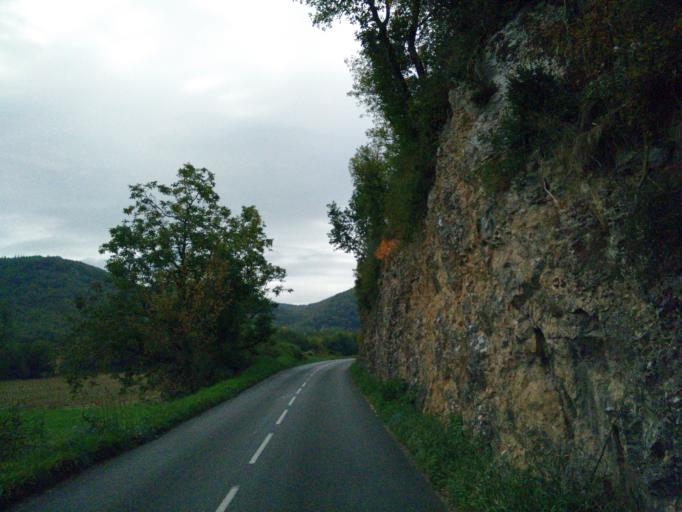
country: FR
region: Midi-Pyrenees
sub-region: Departement du Lot
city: Lalbenque
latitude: 44.4713
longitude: 1.6048
